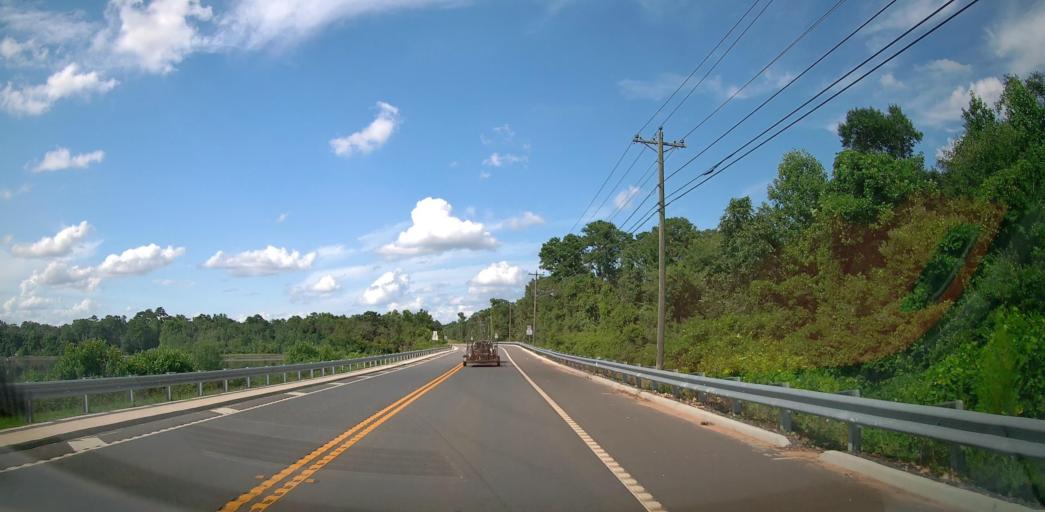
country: US
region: Georgia
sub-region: Houston County
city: Perry
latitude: 32.5099
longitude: -83.6950
